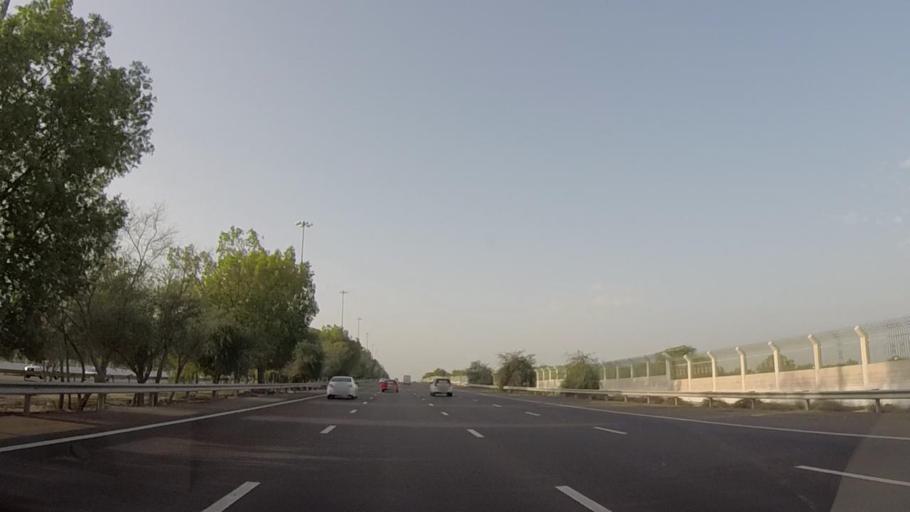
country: AE
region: Dubai
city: Dubai
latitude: 24.8378
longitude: 54.8878
